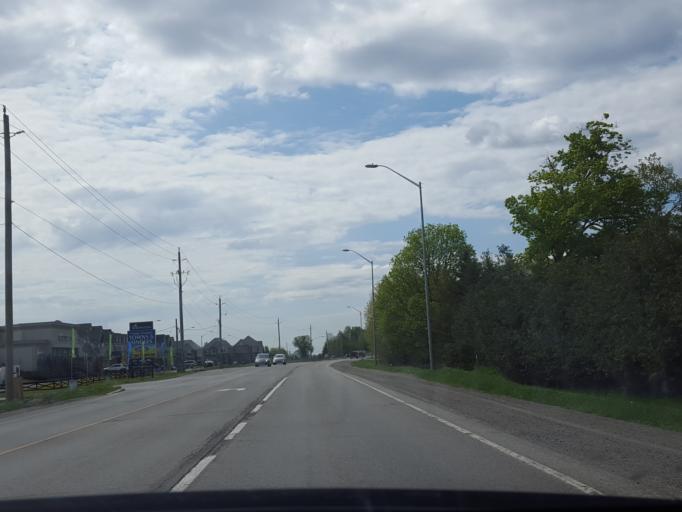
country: CA
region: Ontario
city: Oshawa
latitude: 43.9371
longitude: -78.7135
